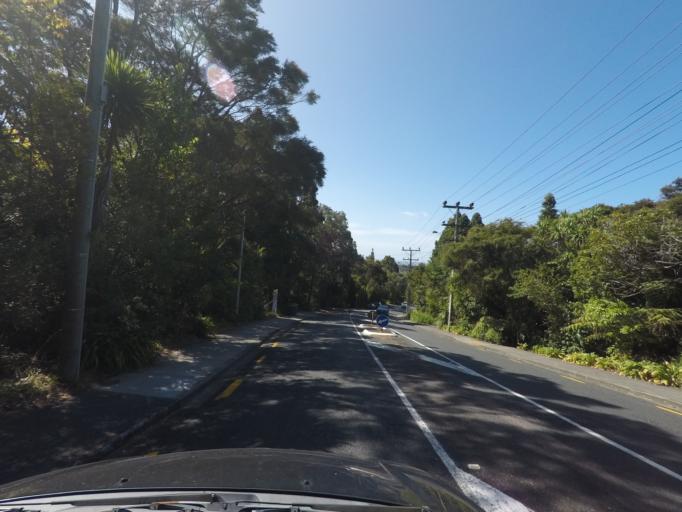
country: NZ
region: Auckland
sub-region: Auckland
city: Titirangi
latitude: -36.9354
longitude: 174.6549
